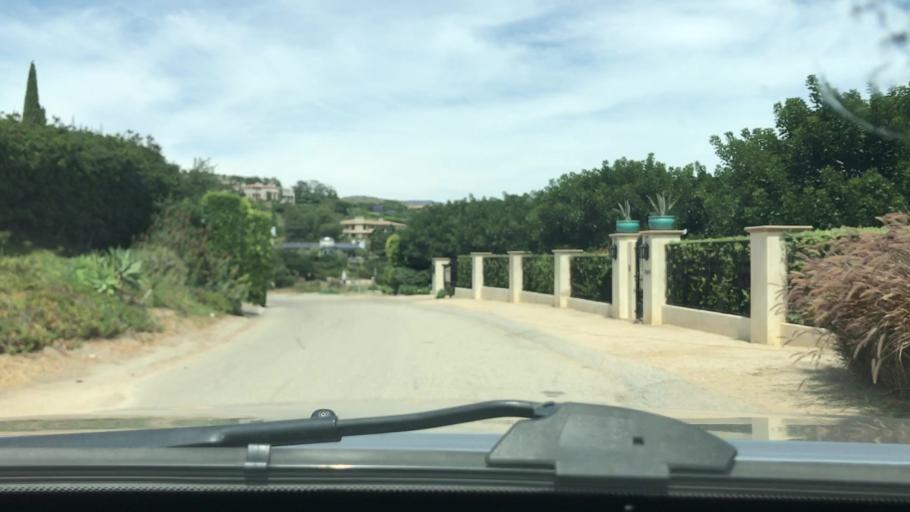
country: US
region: California
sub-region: Los Angeles County
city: Malibu
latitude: 34.0280
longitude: -118.7821
